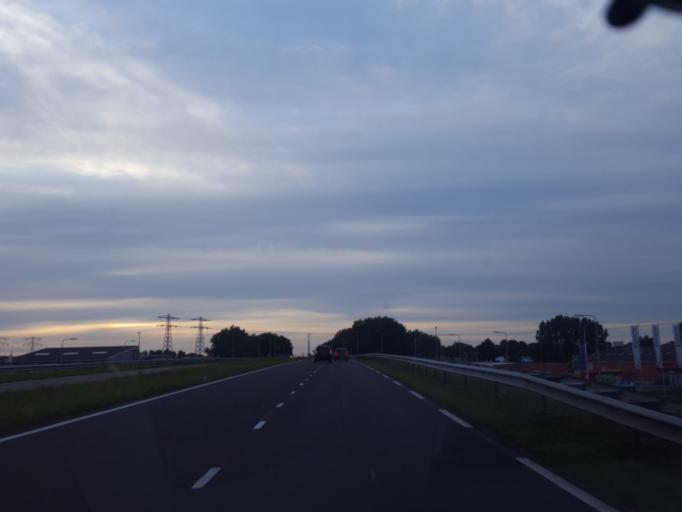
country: NL
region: Friesland
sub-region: Gemeente Leeuwarden
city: Camminghaburen
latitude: 53.1976
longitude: 5.8390
